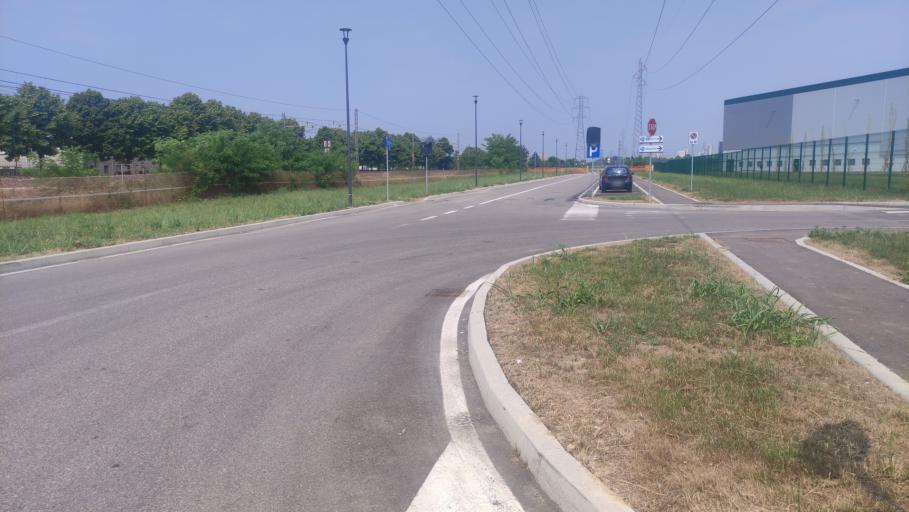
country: IT
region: Emilia-Romagna
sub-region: Provincia di Piacenza
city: Piacenza
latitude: 45.0324
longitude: 9.7407
